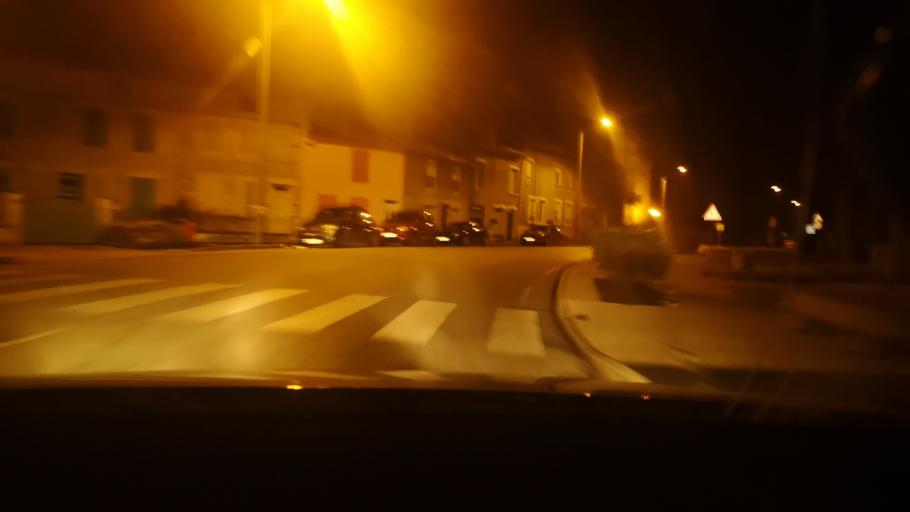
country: FR
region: Rhone-Alpes
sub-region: Departement de l'Ain
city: Saint-Trivier-de-Courtes
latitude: 46.4017
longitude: 5.1097
